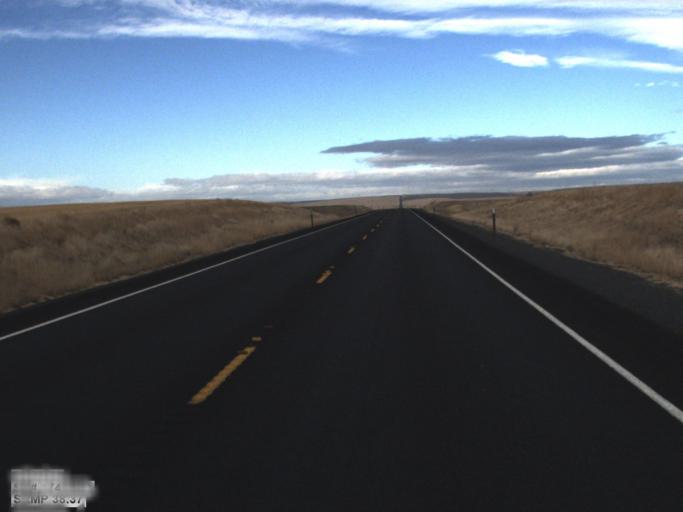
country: US
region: Washington
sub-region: Okanogan County
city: Coulee Dam
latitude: 47.7972
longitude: -118.7526
